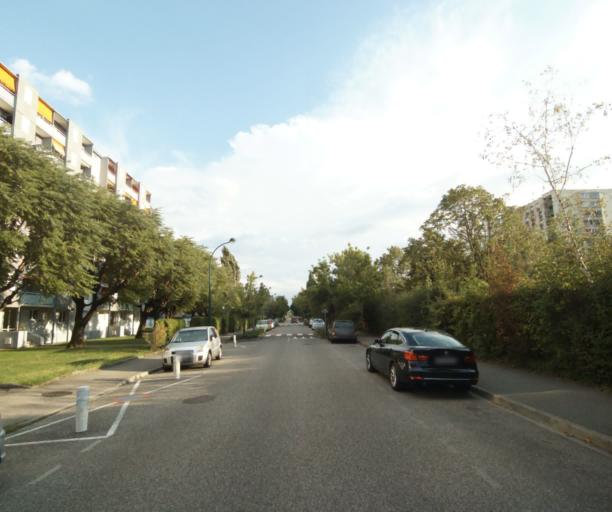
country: FR
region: Rhone-Alpes
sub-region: Departement de l'Isere
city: Seyssinet-Pariset
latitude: 45.1714
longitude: 5.6968
